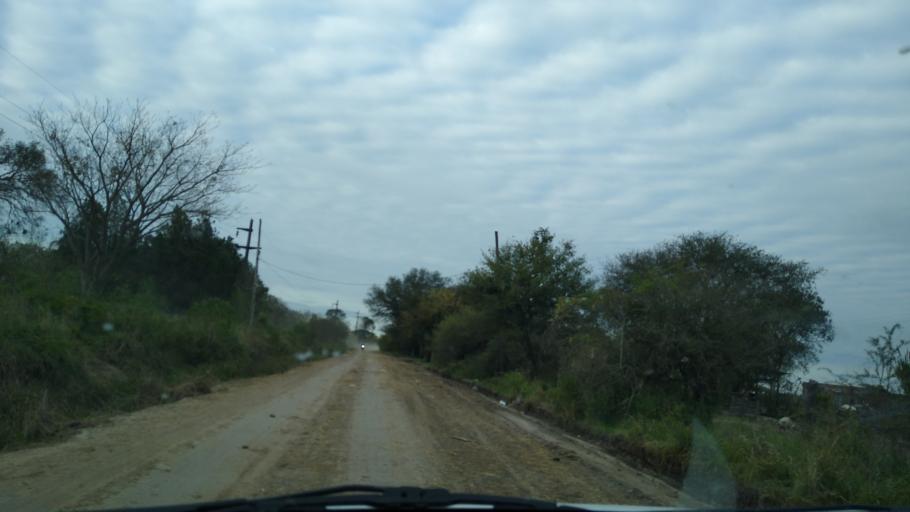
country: AR
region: Chaco
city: Fontana
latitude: -27.3828
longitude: -59.0413
